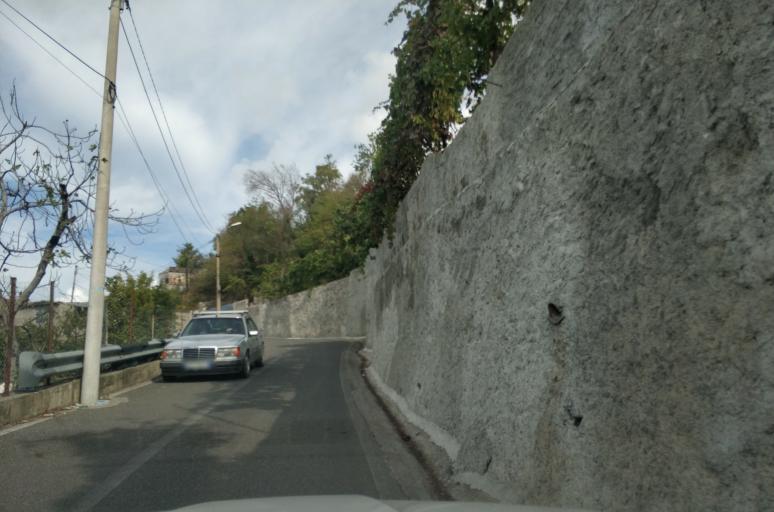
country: AL
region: Durres
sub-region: Rrethi i Krujes
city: Kruje
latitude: 41.5131
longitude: 19.7947
